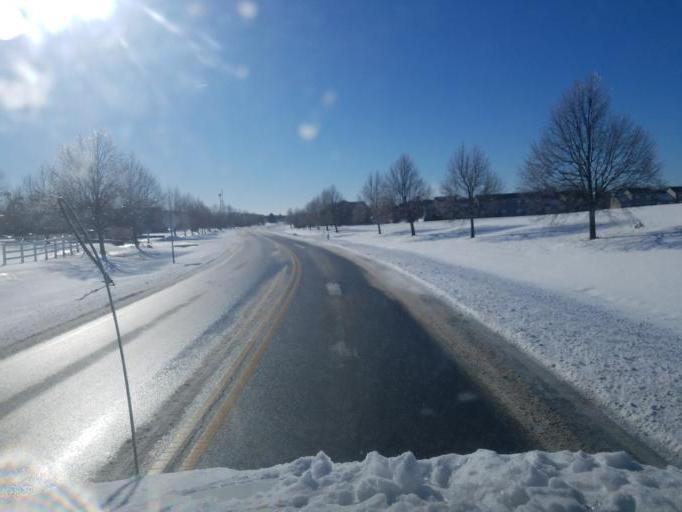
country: US
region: Ohio
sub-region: Delaware County
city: Lewis Center
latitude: 40.1732
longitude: -83.0106
